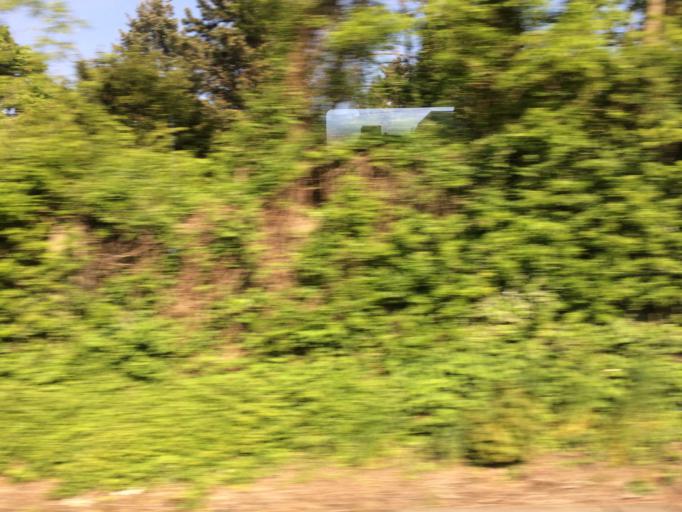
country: DE
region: North Rhine-Westphalia
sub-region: Regierungsbezirk Dusseldorf
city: Dusseldorf
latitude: 51.2466
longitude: 6.7950
